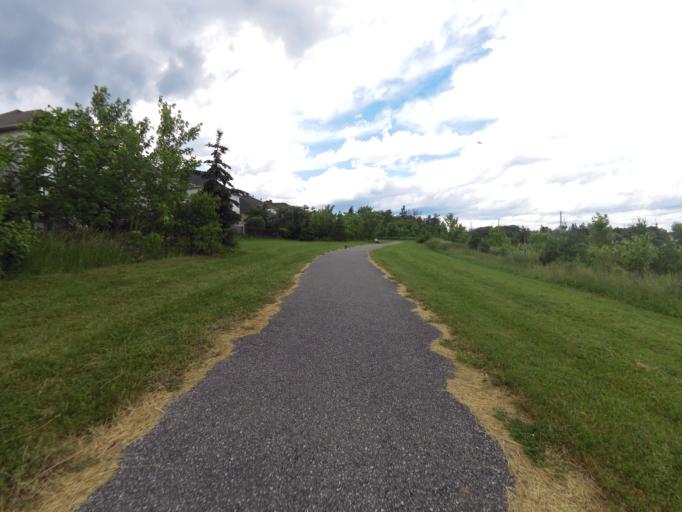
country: CA
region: Ontario
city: Ottawa
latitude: 45.2884
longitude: -75.7030
